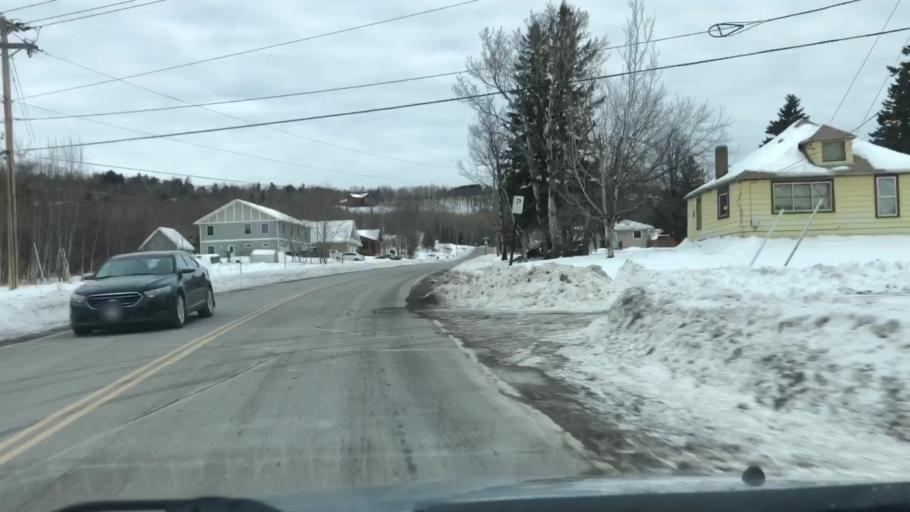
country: US
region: Minnesota
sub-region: Saint Louis County
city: Arnold
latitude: 46.8366
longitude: -92.0370
